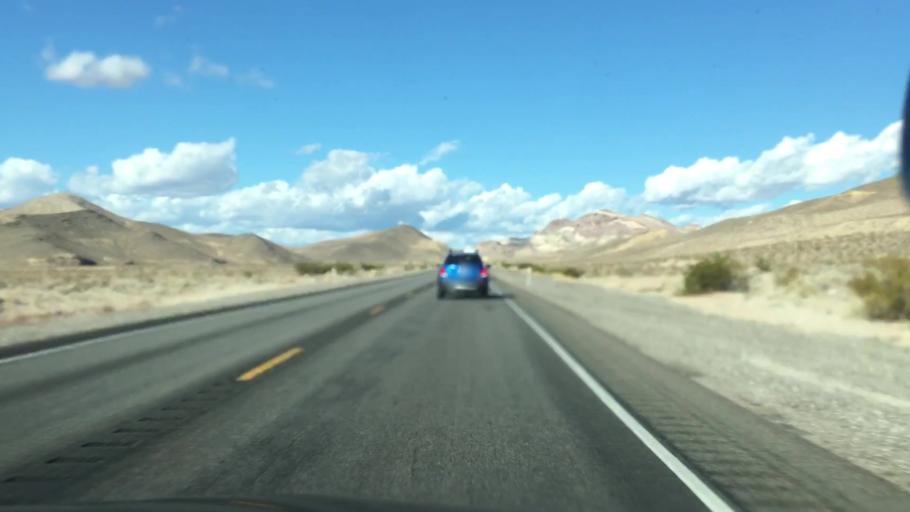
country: US
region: Nevada
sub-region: Nye County
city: Beatty
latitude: 36.8621
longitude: -116.7567
